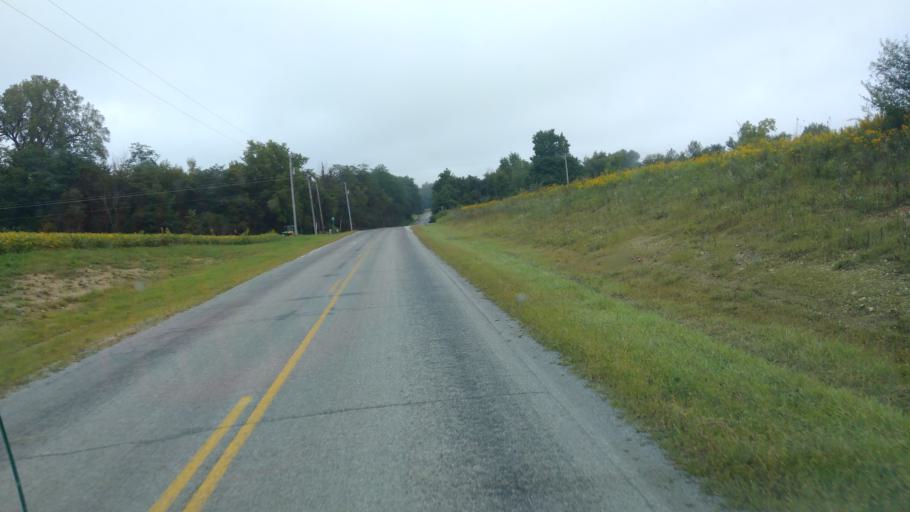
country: US
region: Ohio
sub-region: Hardin County
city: Kenton
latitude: 40.5730
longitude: -83.6333
